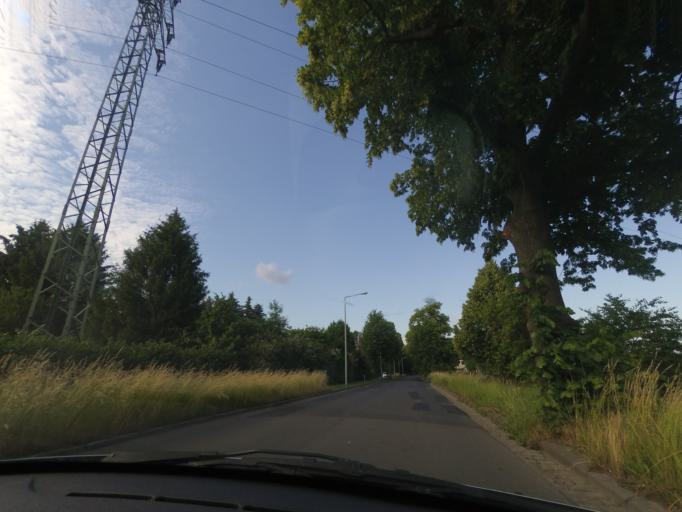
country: DE
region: Saxony
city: Heidenau
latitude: 50.9929
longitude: 13.8153
